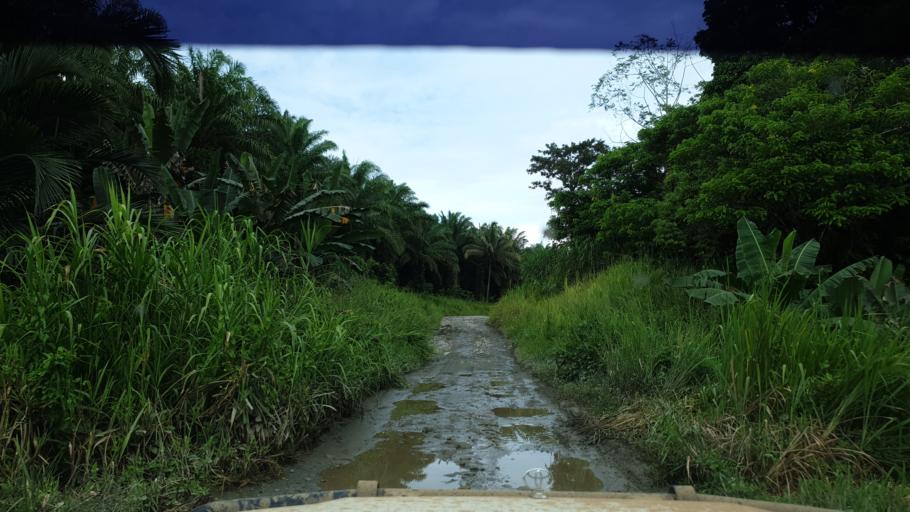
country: PG
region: Northern Province
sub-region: Sohe
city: Kokoda
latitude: -8.9172
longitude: 147.8609
